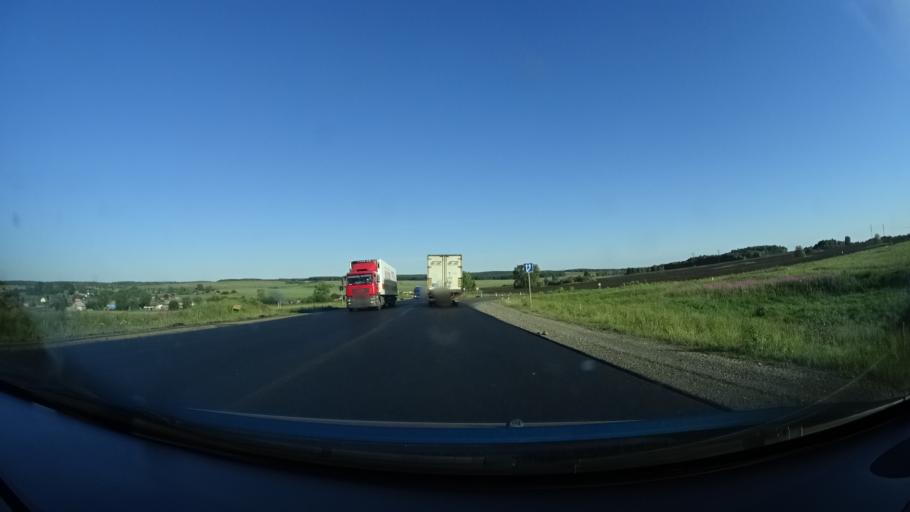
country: RU
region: Sverdlovsk
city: Achit
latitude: 56.8958
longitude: 57.6033
